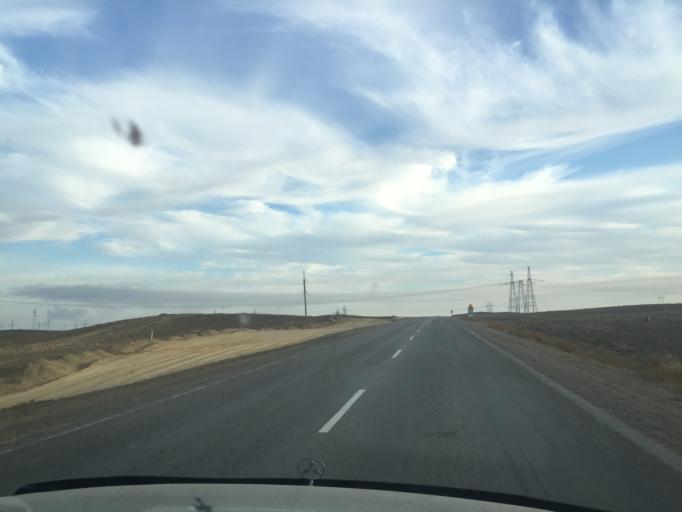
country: KZ
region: Almaty Oblysy
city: Ulken
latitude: 45.1461
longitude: 73.9568
